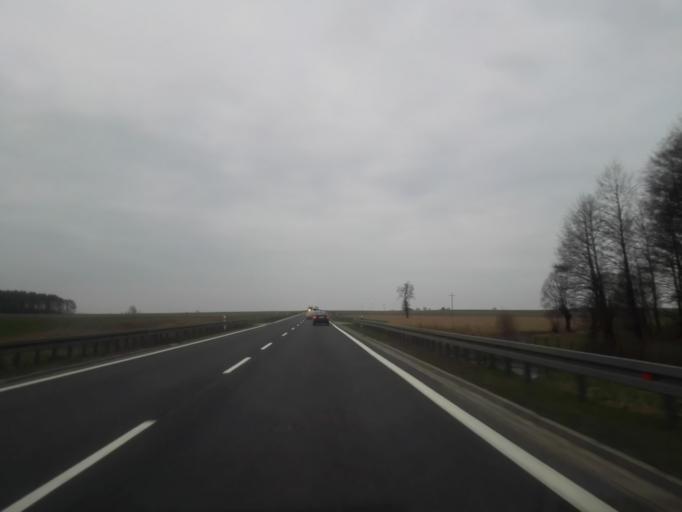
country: PL
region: Podlasie
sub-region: Powiat kolnenski
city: Stawiski
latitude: 53.4166
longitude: 22.1644
